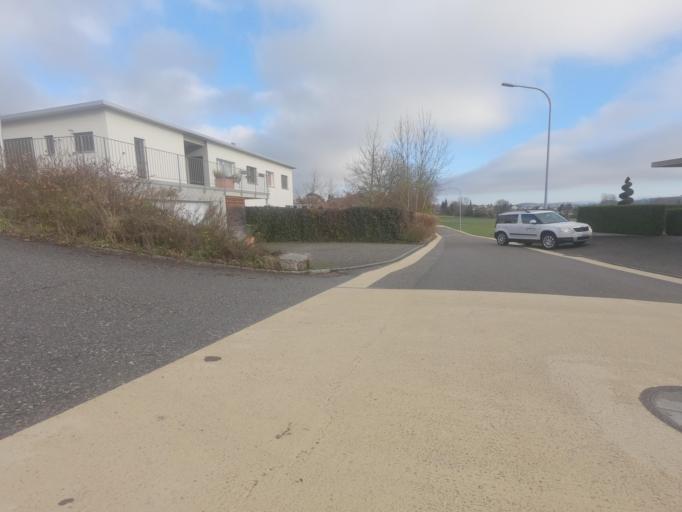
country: CH
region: Solothurn
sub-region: Bezirk Lebern
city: Langendorf
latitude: 47.2120
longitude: 7.4856
